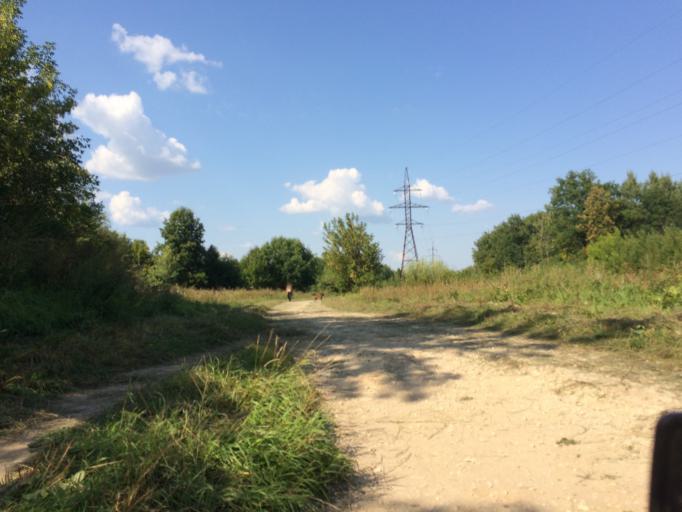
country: RU
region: Mariy-El
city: Yoshkar-Ola
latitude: 56.6135
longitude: 47.9319
